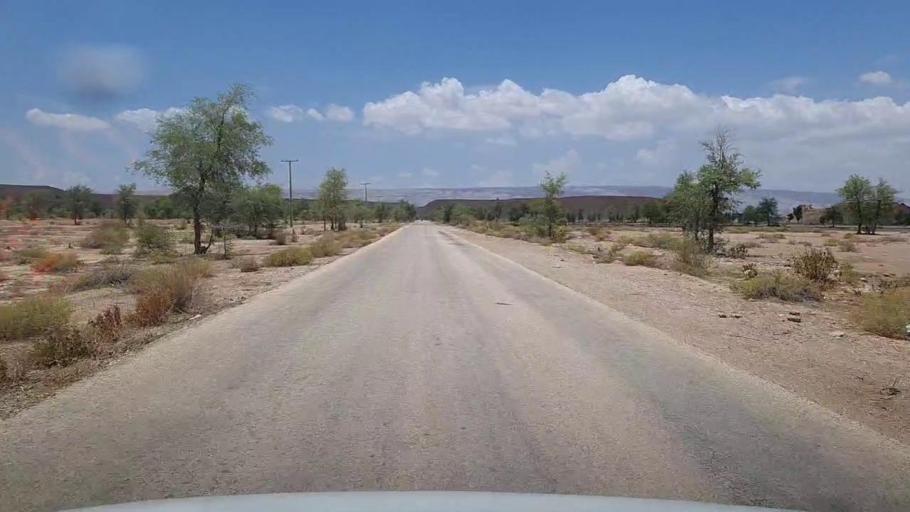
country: PK
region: Sindh
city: Bhan
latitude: 26.3173
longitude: 67.5963
